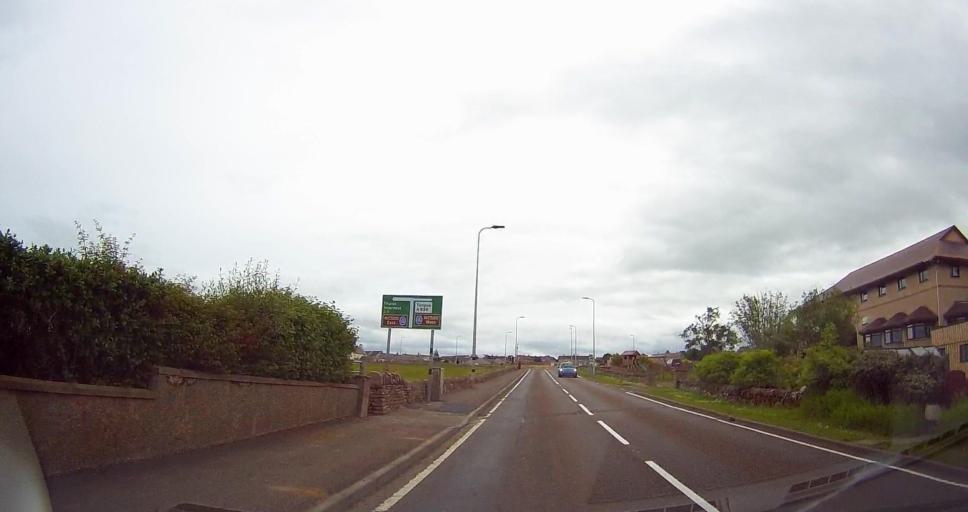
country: GB
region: Scotland
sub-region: Highland
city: Thurso
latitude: 58.5995
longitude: -3.5389
